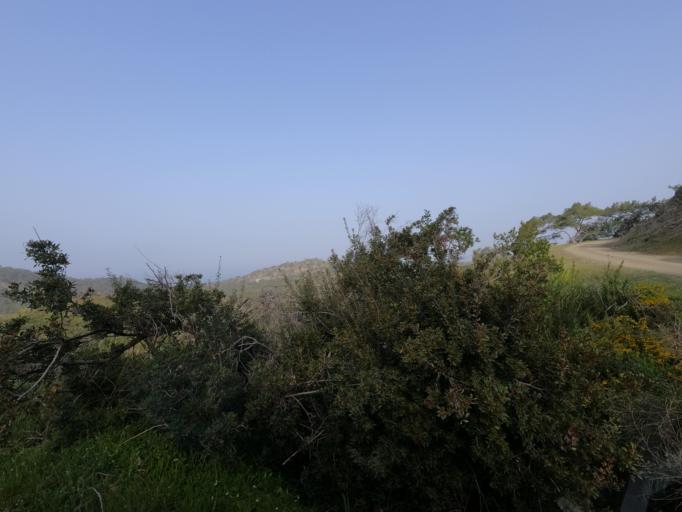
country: CY
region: Pafos
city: Polis
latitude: 35.0011
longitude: 32.3361
